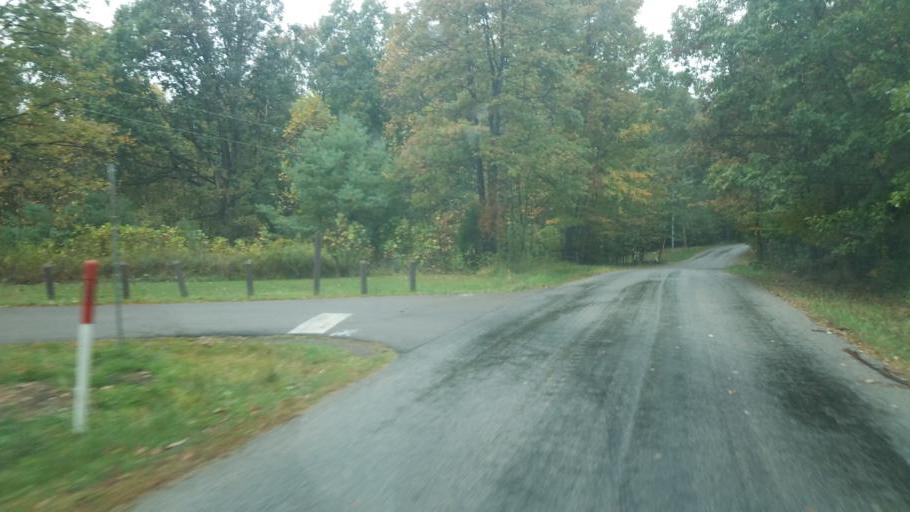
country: US
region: Ohio
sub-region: Ashland County
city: Loudonville
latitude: 40.6051
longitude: -82.3049
